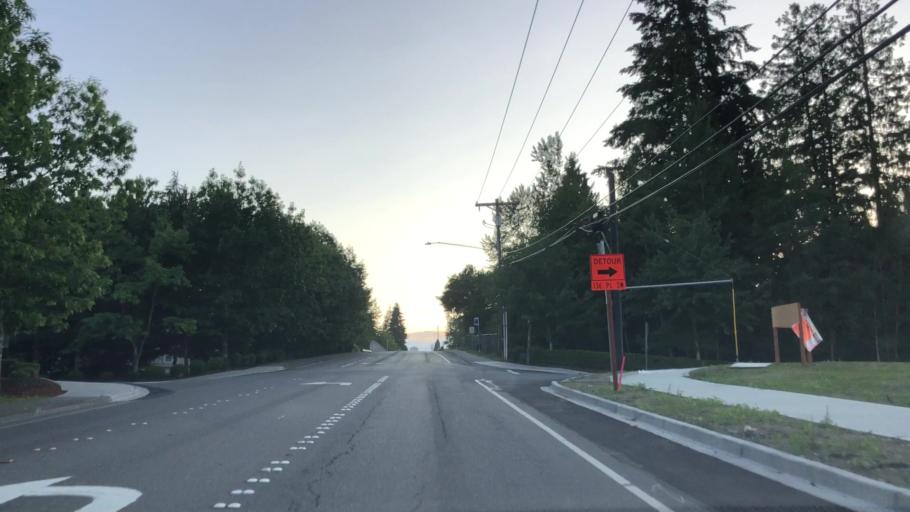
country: US
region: Washington
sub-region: Snohomish County
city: Martha Lake
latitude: 47.8642
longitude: -122.2722
